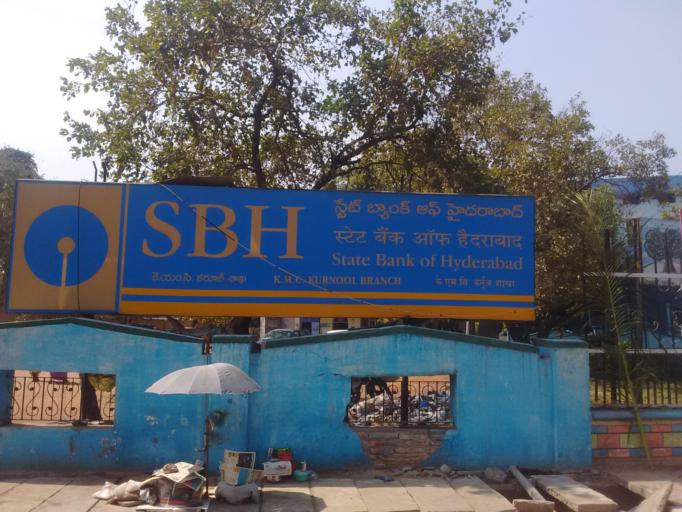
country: IN
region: Telangana
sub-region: Mahbubnagar
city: Alampur
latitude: 15.8365
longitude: 78.0412
